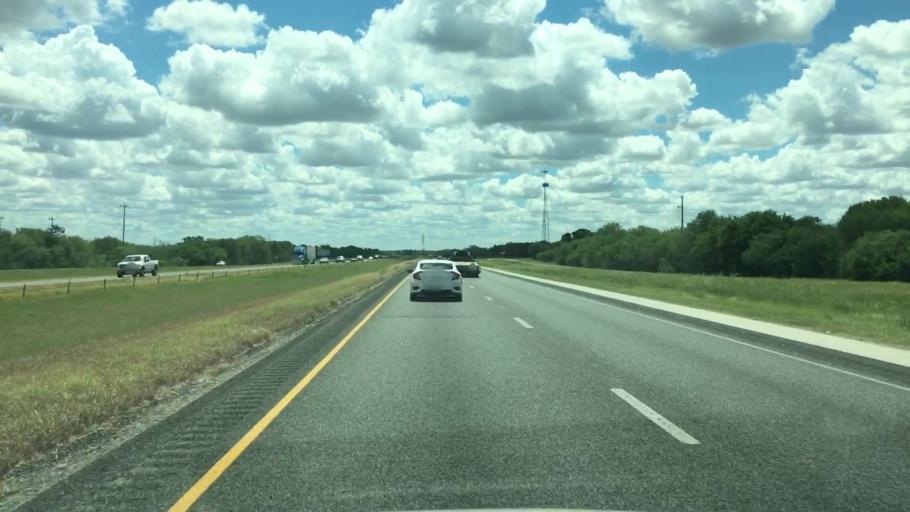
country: US
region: Texas
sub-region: Bexar County
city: Elmendorf
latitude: 29.2642
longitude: -98.3957
